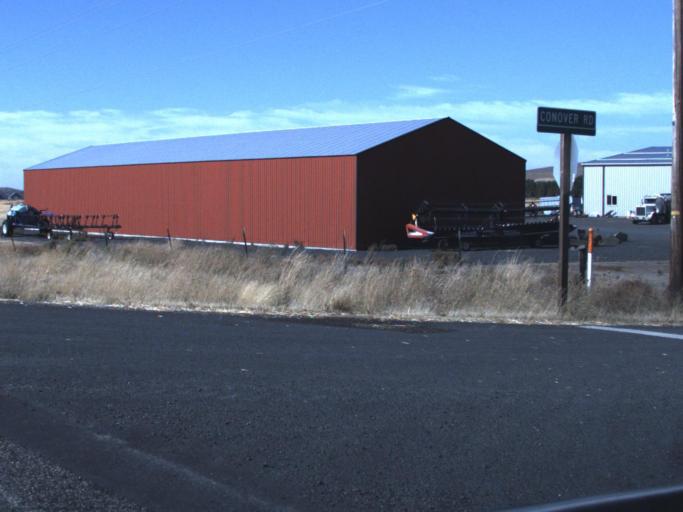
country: US
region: Washington
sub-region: Walla Walla County
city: Waitsburg
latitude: 46.2666
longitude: -118.2002
